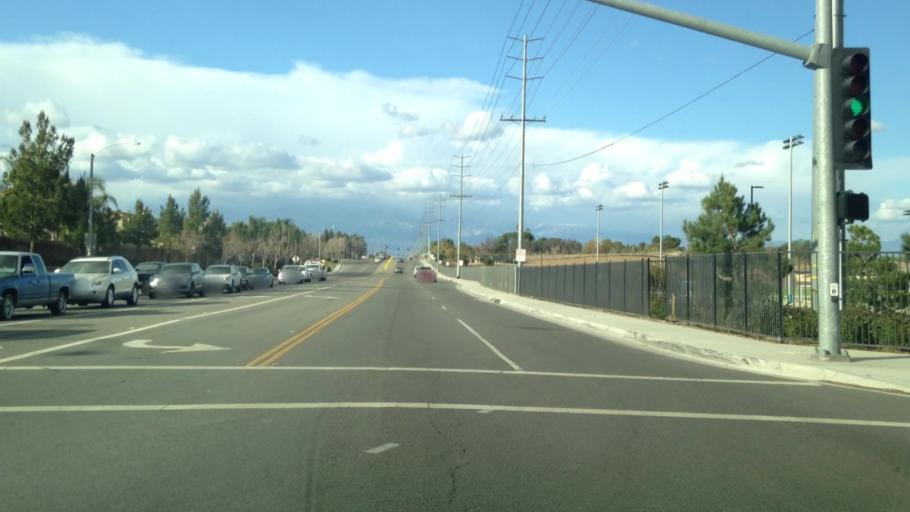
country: US
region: California
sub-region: Riverside County
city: Norco
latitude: 33.9519
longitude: -117.5583
